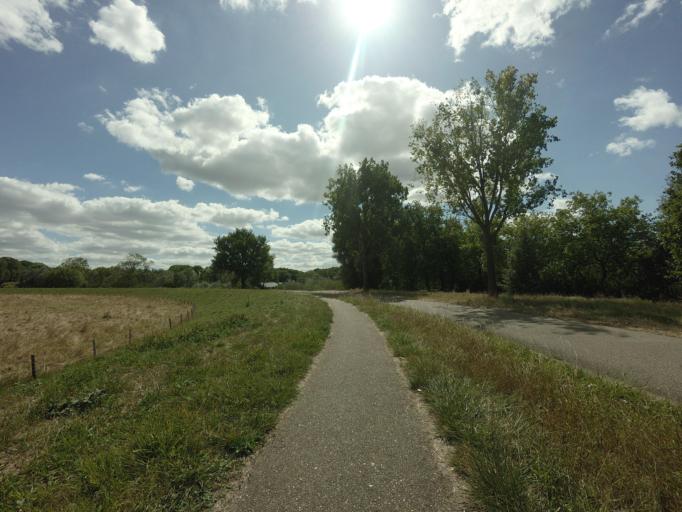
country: NL
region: Gelderland
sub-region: Gemeente Wijchen
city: Bergharen
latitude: 51.8191
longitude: 5.6150
